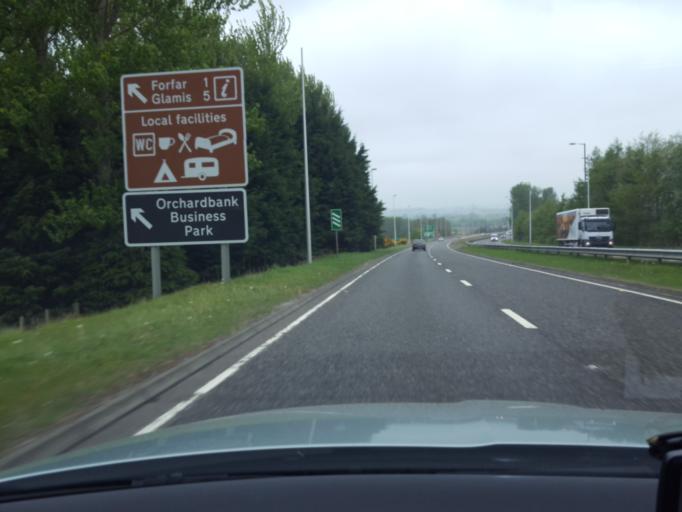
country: GB
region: Scotland
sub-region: Angus
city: Forfar
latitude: 56.6290
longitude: -2.9200
